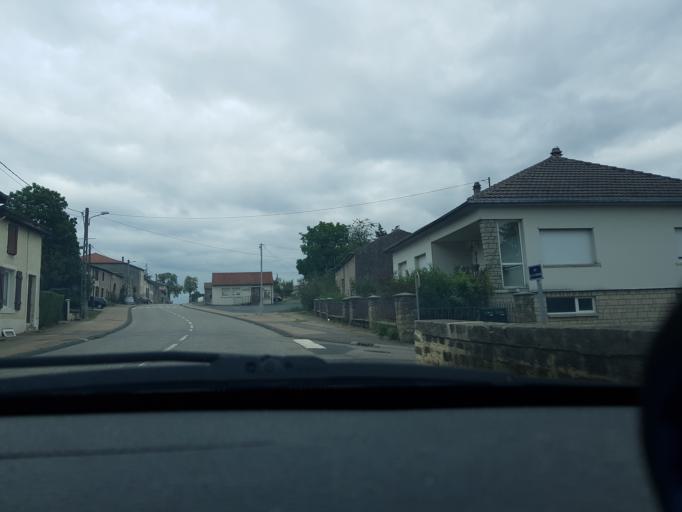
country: FR
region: Lorraine
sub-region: Departement de la Moselle
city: Chateau-Salins
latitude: 48.8520
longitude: 6.5144
